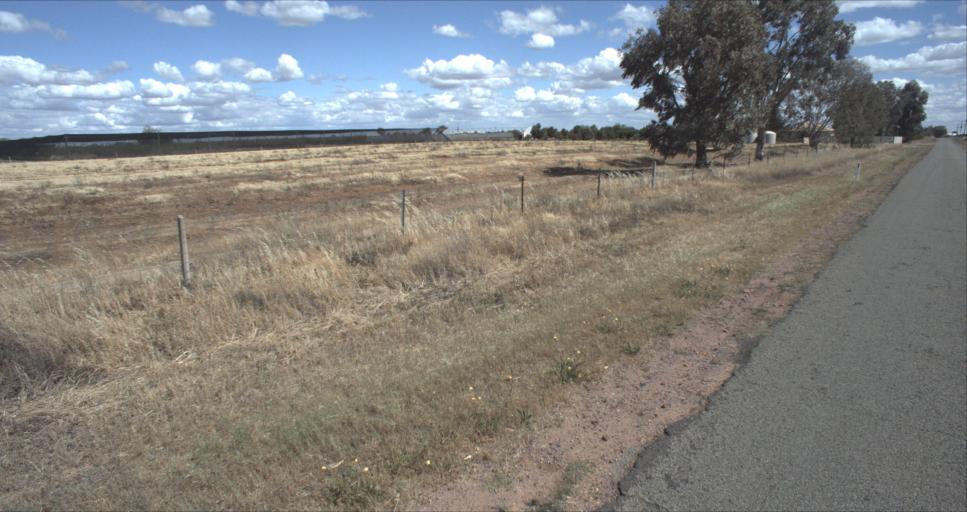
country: AU
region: New South Wales
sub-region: Leeton
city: Leeton
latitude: -34.5152
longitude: 146.2385
